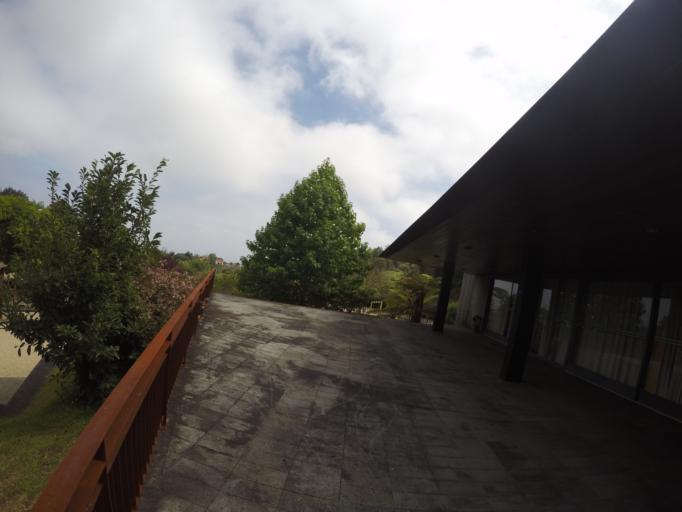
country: PT
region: Madeira
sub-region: Santana
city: Santana
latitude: 32.8019
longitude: -16.8853
